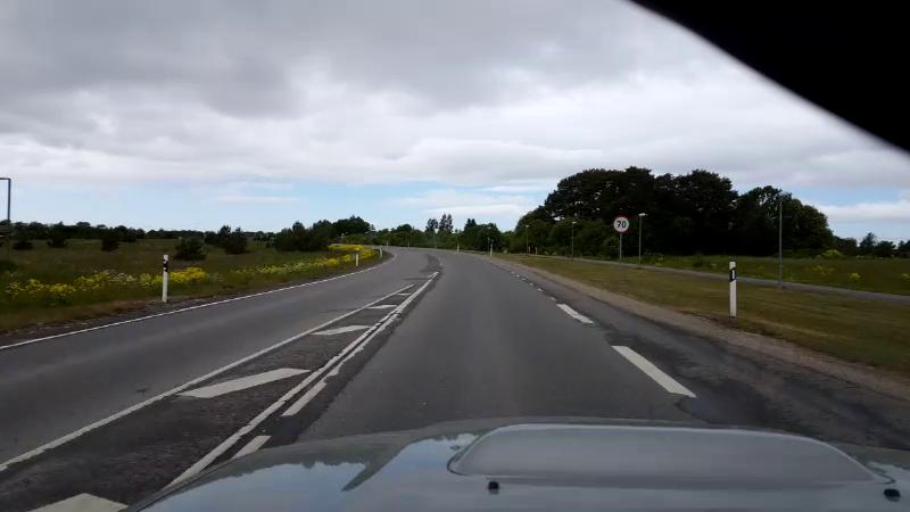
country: EE
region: Harju
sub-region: Harku vald
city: Tabasalu
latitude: 59.4529
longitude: 24.4539
